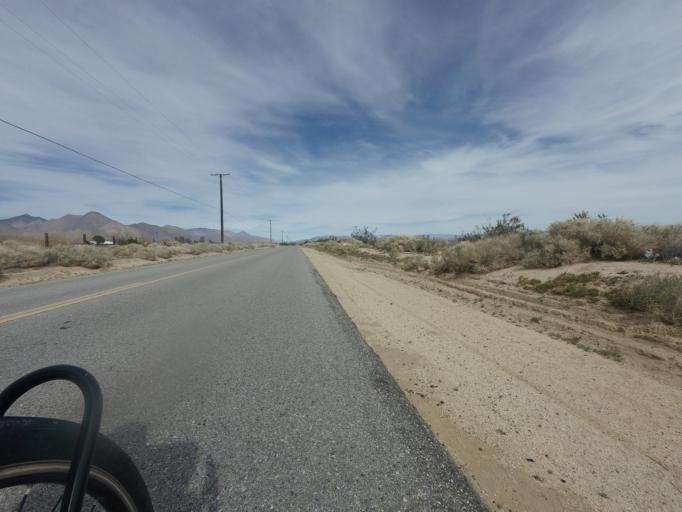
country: US
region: California
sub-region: Kern County
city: Inyokern
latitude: 35.7288
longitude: -117.8366
